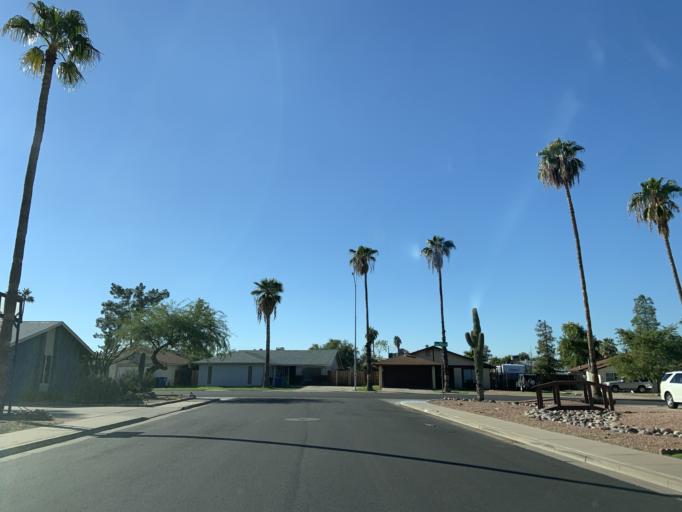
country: US
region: Arizona
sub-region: Maricopa County
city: Tempe
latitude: 33.3981
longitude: -111.8802
